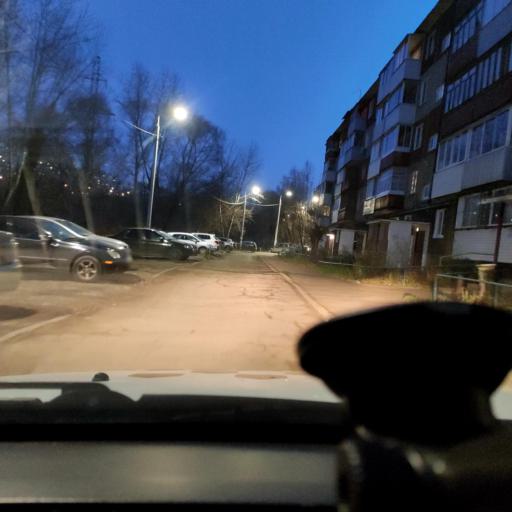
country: RU
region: Perm
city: Perm
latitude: 57.9926
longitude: 56.2333
